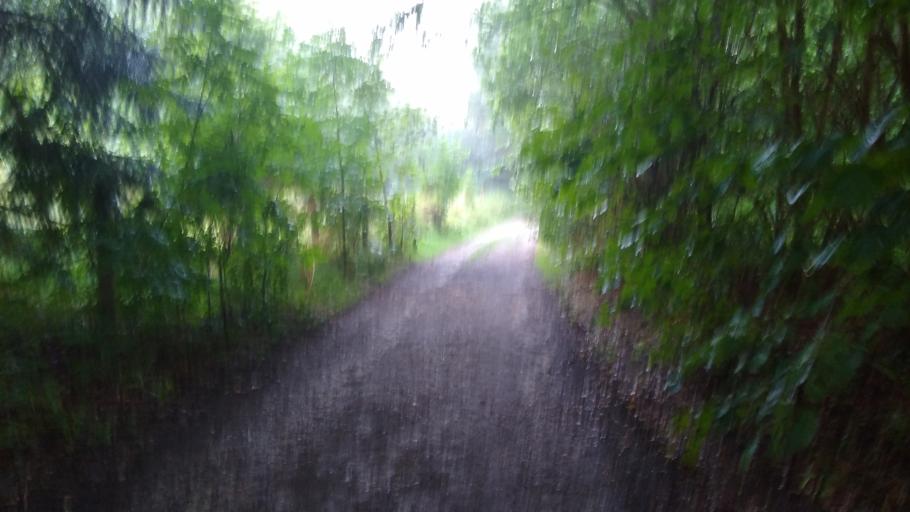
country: DK
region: South Denmark
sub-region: Fredericia Kommune
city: Fredericia
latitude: 55.6053
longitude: 9.7087
